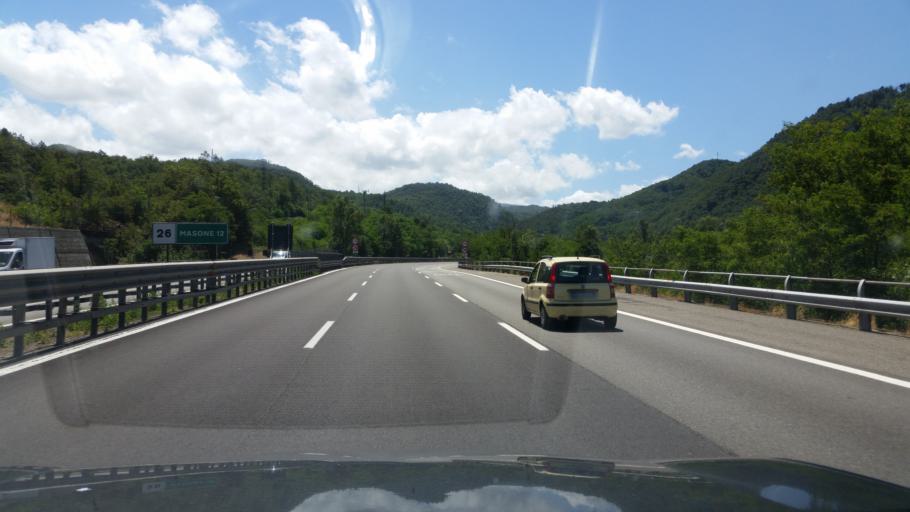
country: IT
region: Piedmont
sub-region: Provincia di Alessandria
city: Belforte Monferrato
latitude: 44.5970
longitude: 8.6671
